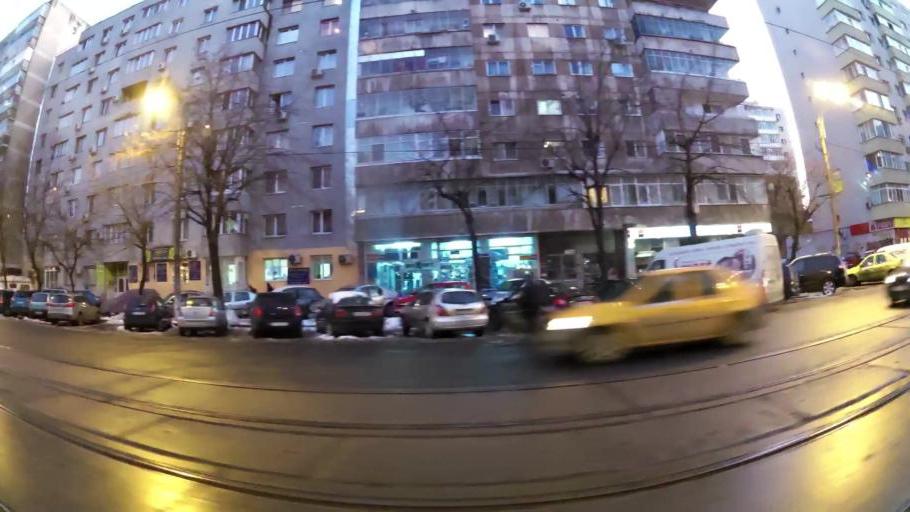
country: RO
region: Ilfov
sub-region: Comuna Fundeni-Dobroesti
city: Fundeni
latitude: 44.4443
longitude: 26.1428
